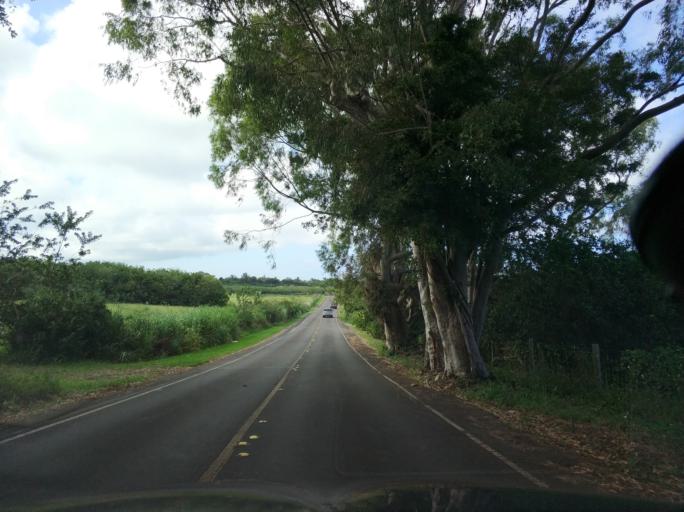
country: US
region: Hawaii
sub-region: Hawaii County
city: Kapaau
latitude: 20.2110
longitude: -155.7410
